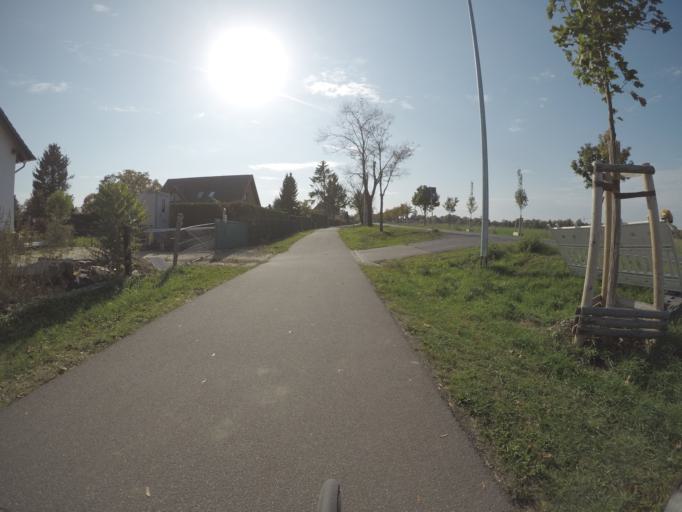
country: DE
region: Brandenburg
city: Velten
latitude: 52.6905
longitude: 13.1967
